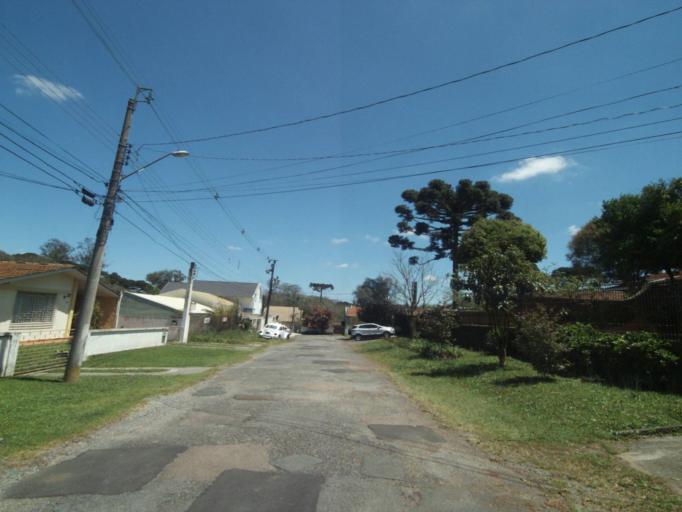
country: BR
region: Parana
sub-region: Curitiba
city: Curitiba
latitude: -25.3922
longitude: -49.2638
